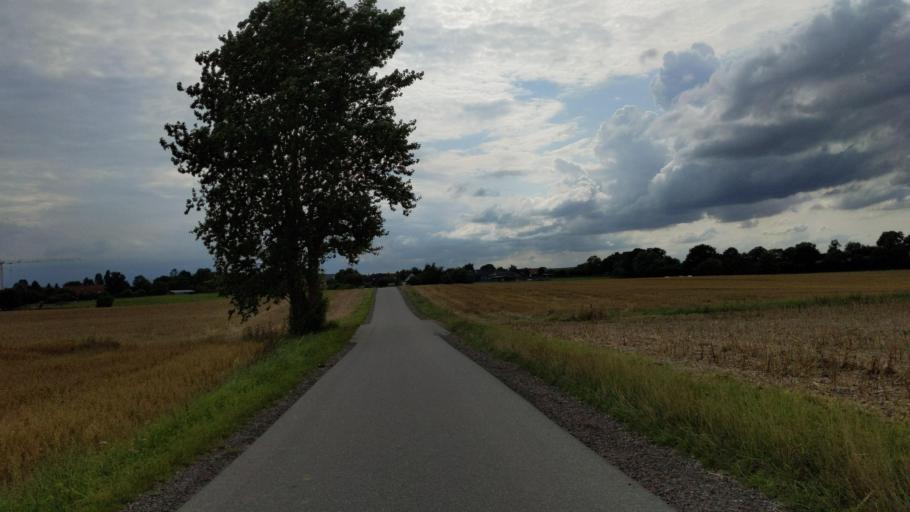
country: DE
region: Schleswig-Holstein
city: Schashagen
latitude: 54.1327
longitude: 10.8647
